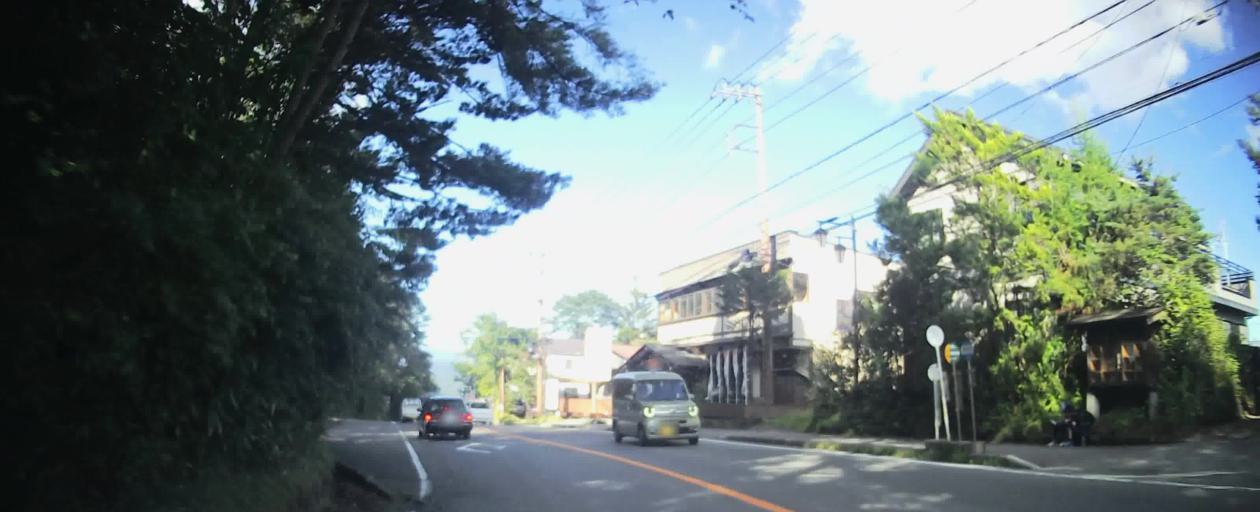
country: JP
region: Gunma
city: Nakanojomachi
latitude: 36.6161
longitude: 138.5923
